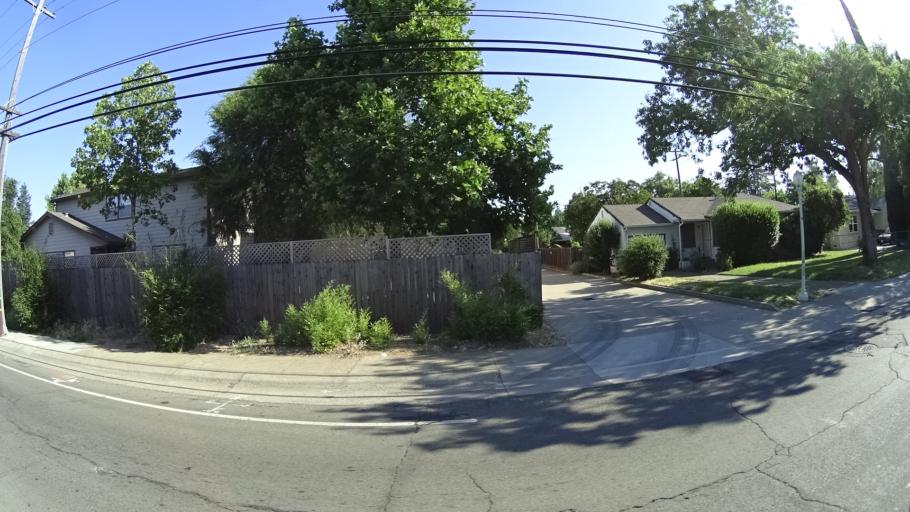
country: US
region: California
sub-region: Sacramento County
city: Parkway
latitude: 38.5395
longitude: -121.4348
